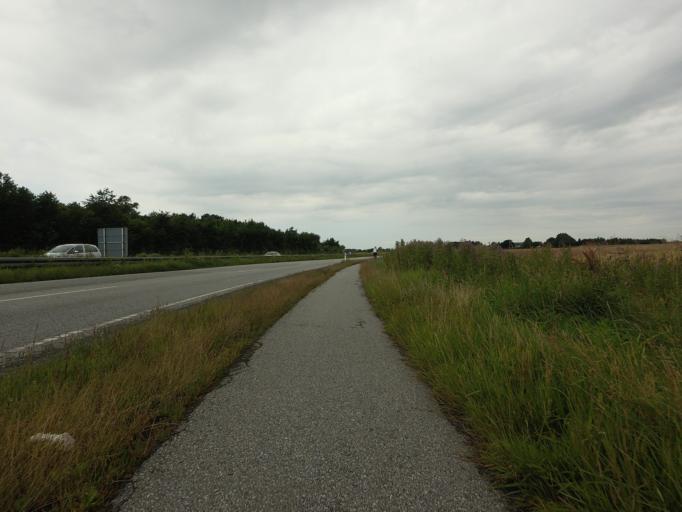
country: DK
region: North Denmark
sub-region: Alborg Kommune
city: Vadum
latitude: 57.1031
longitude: 9.8839
